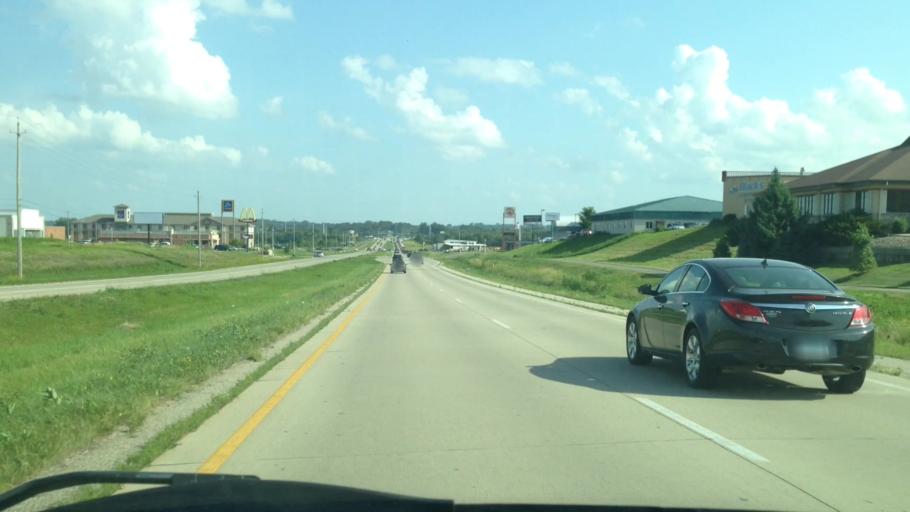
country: US
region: Minnesota
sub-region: Olmsted County
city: Rochester
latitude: 44.0495
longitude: -92.5219
